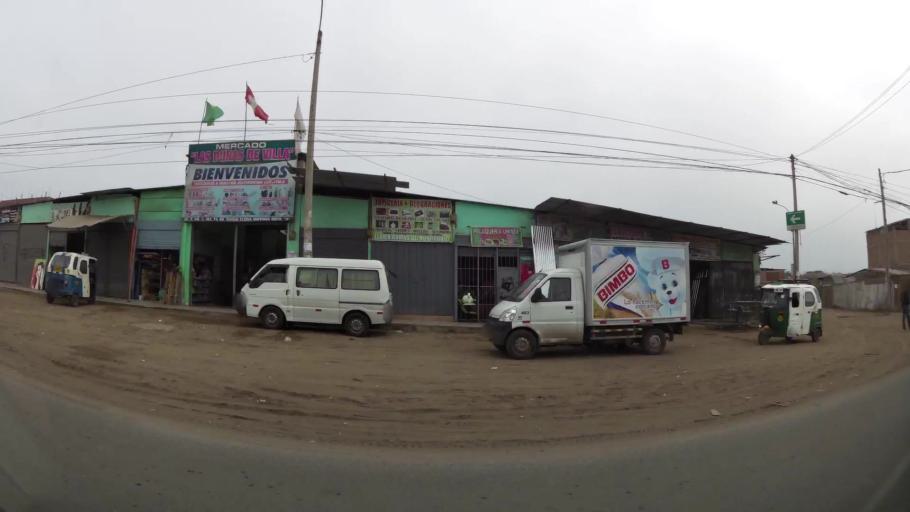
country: PE
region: Lima
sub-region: Lima
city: Surco
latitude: -12.2353
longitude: -76.9399
